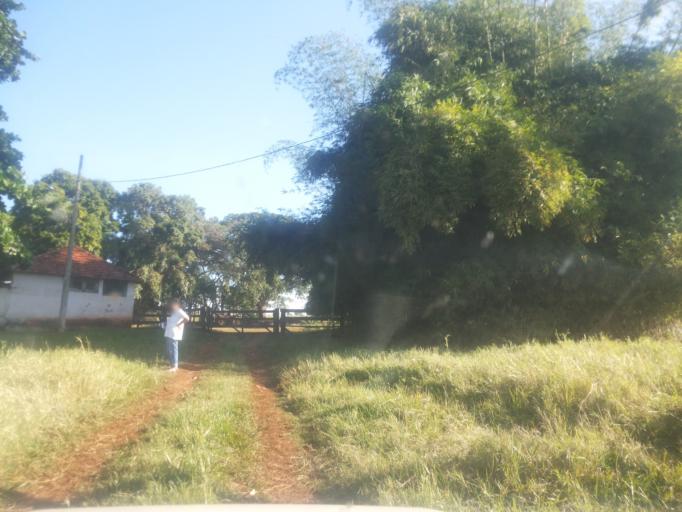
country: BR
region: Minas Gerais
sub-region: Santa Vitoria
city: Santa Vitoria
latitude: -18.9988
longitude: -50.4488
